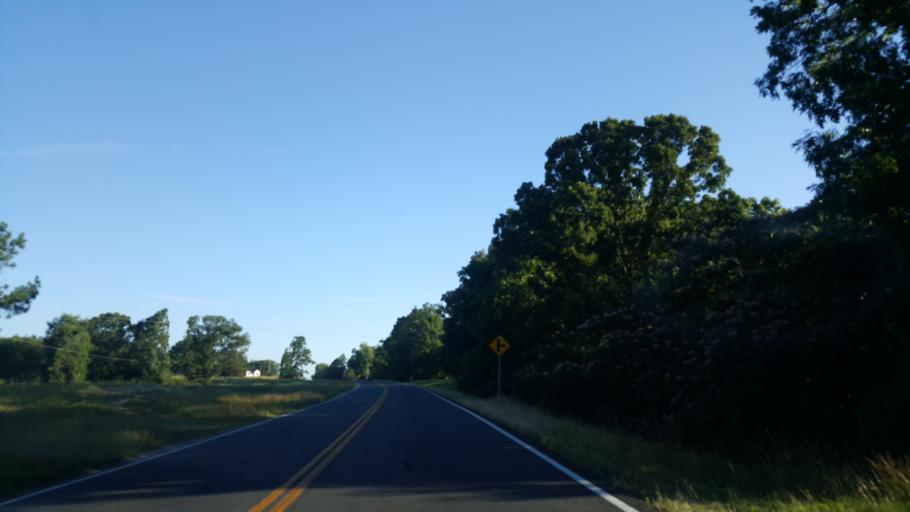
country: US
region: Tennessee
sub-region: Henderson County
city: Lexington
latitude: 35.5984
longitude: -88.3898
